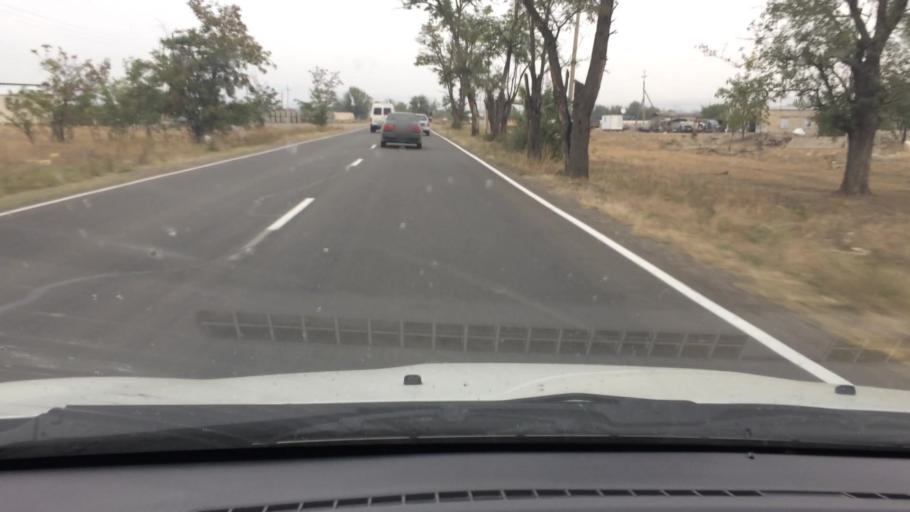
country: GE
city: Naghvarevi
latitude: 41.3902
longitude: 44.8284
